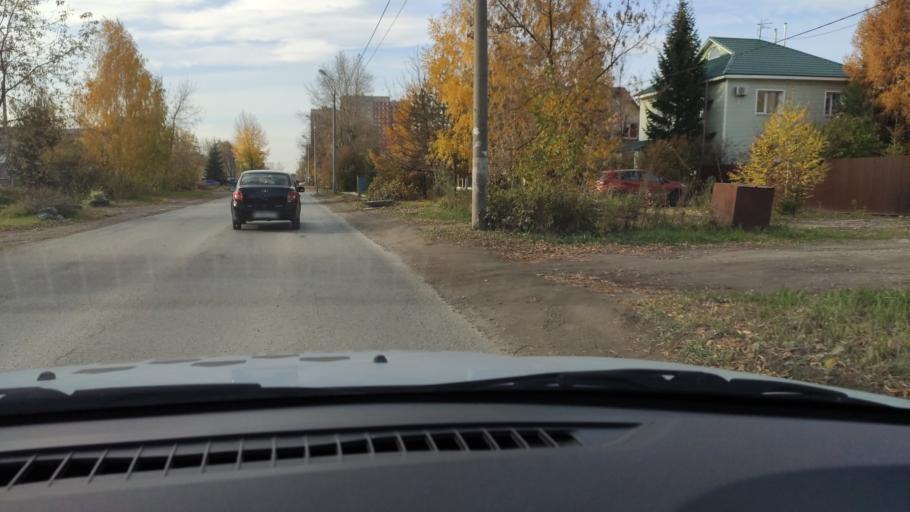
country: RU
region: Perm
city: Perm
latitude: 57.9902
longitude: 56.3032
